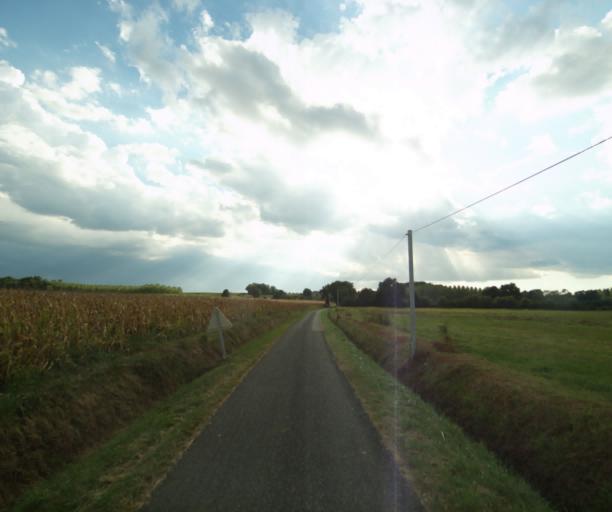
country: FR
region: Midi-Pyrenees
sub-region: Departement du Gers
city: Cazaubon
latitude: 43.9051
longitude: -0.0562
